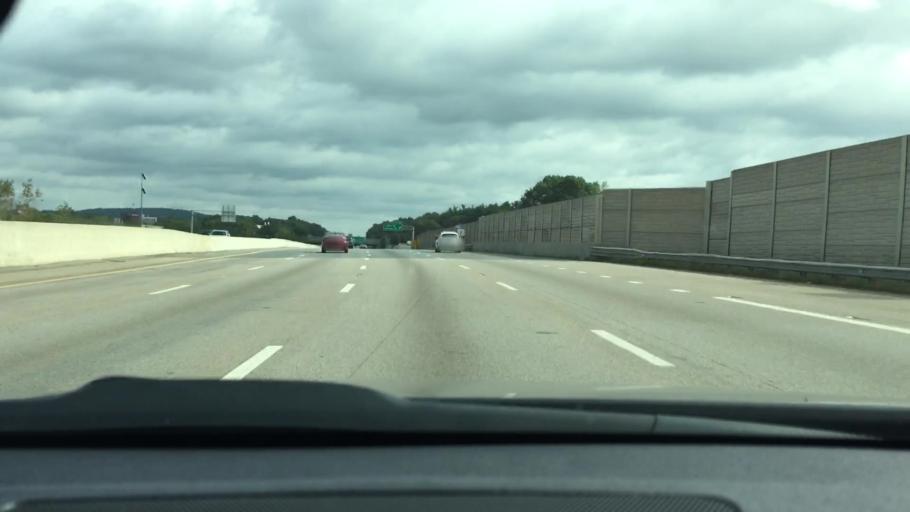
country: US
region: Massachusetts
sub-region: Norfolk County
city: Dedham
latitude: 42.2260
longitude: -71.1786
